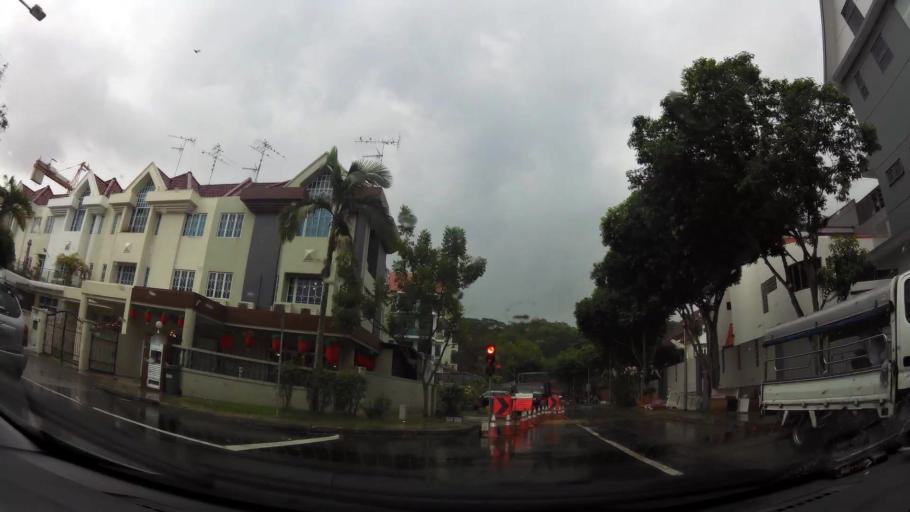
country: MY
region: Johor
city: Kampung Pasir Gudang Baru
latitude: 1.3913
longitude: 103.8514
